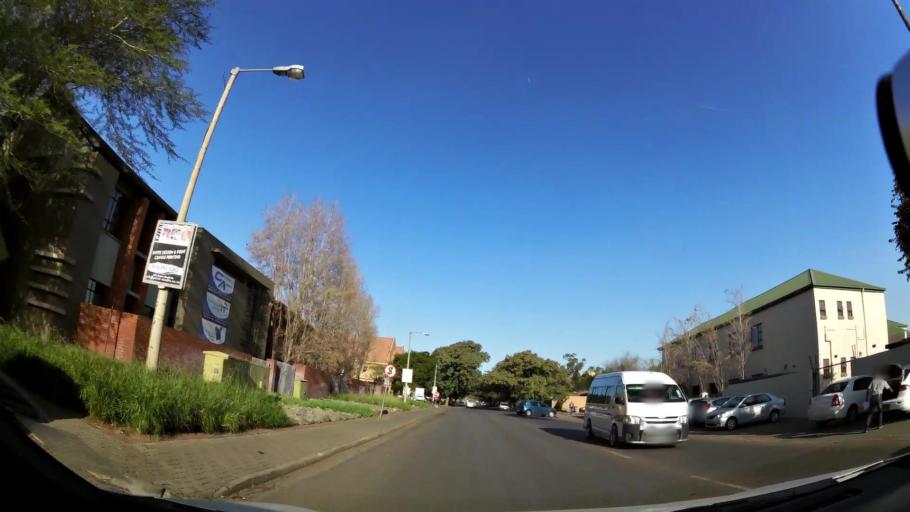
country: ZA
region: North-West
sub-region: Bojanala Platinum District Municipality
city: Rustenburg
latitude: -25.6716
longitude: 27.2384
